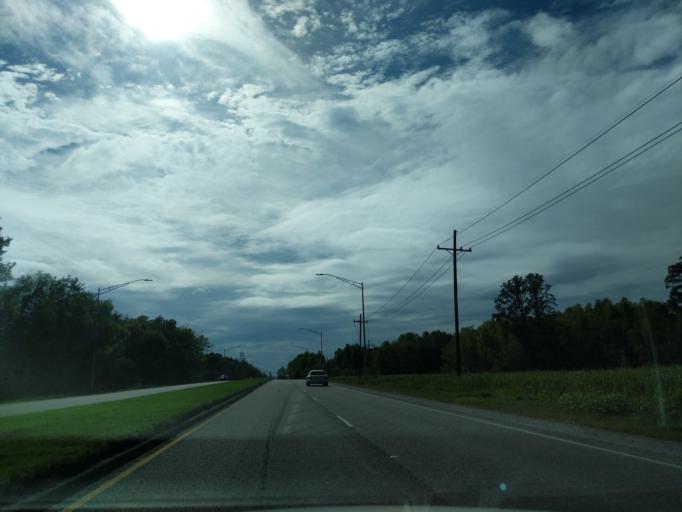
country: US
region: Louisiana
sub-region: Saint Bernard Parish
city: Chalmette
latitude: 30.0399
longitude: -89.9007
